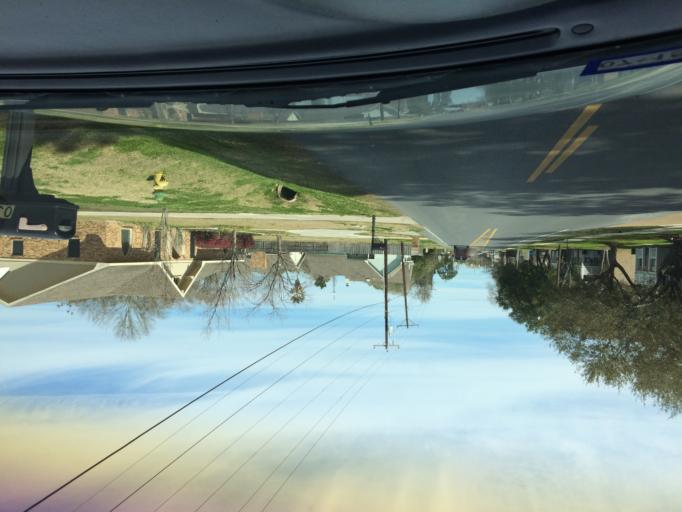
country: US
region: Louisiana
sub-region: Lafayette Parish
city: Scott
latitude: 30.2125
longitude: -92.0614
